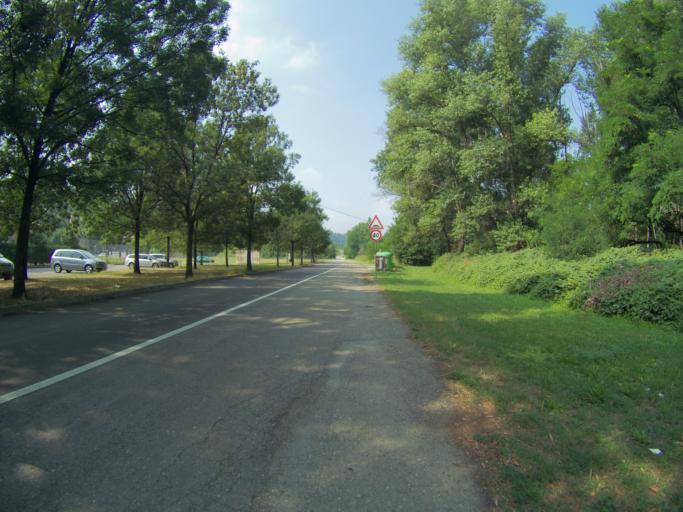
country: IT
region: Emilia-Romagna
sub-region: Provincia di Reggio Emilia
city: Ventoso
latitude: 44.5867
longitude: 10.6718
